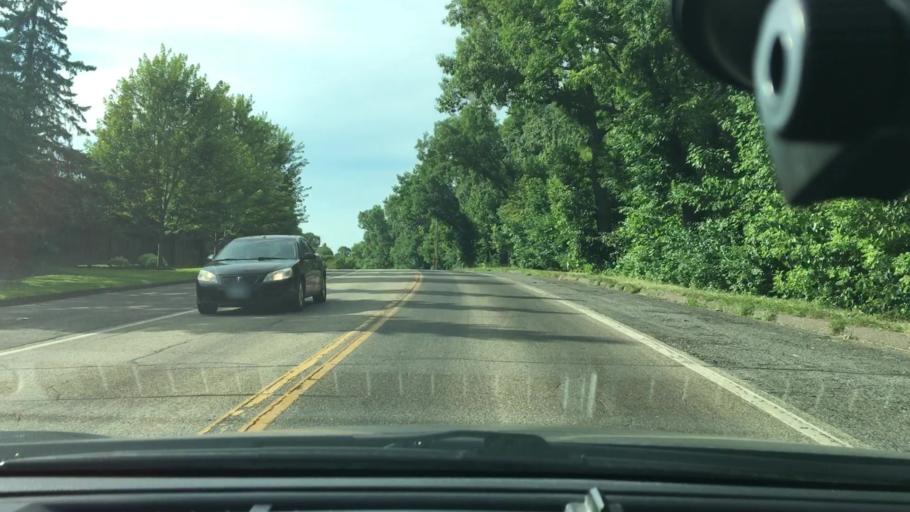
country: US
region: Minnesota
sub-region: Hennepin County
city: Plymouth
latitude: 45.0154
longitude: -93.4398
